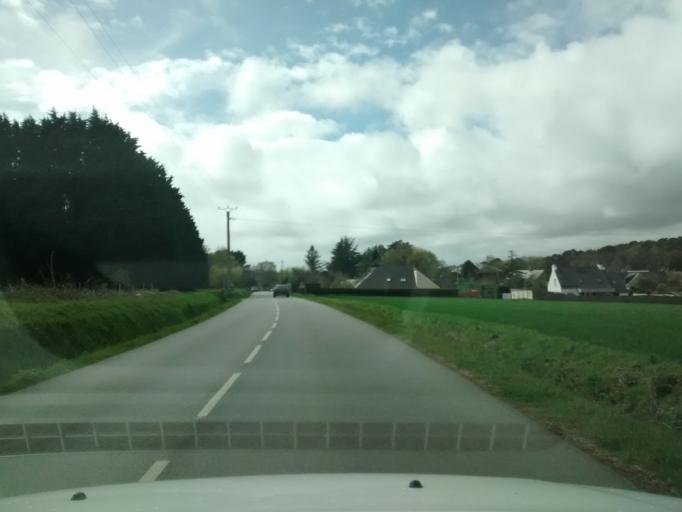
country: FR
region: Brittany
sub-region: Departement du Morbihan
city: Guidel-Plage
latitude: 47.7947
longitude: -3.5120
